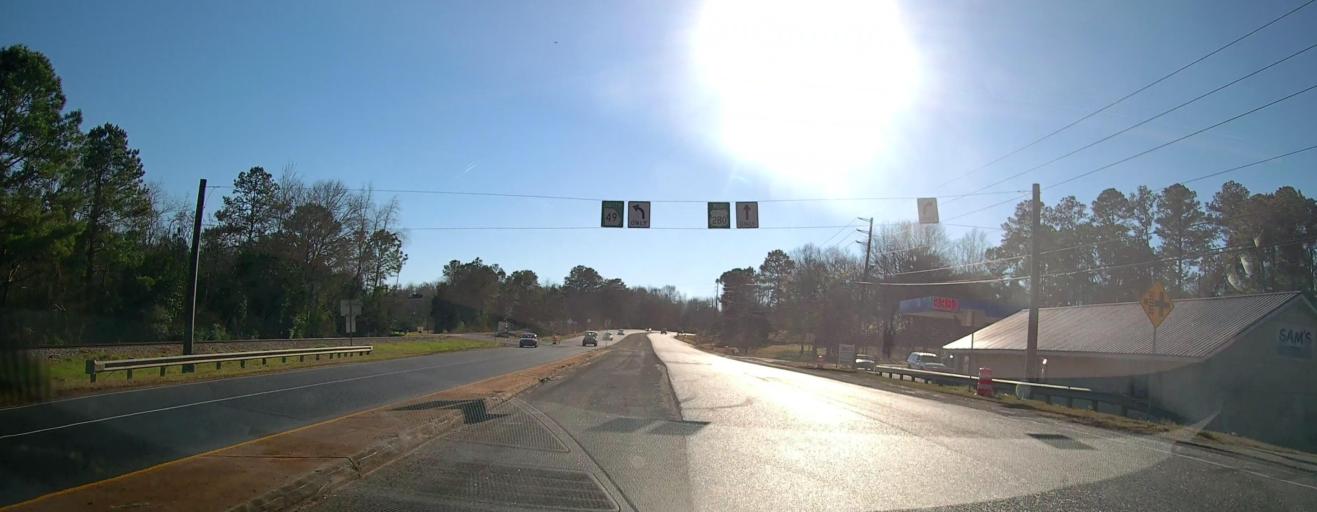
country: US
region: Georgia
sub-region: Sumter County
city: Americus
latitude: 32.0607
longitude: -84.2682
